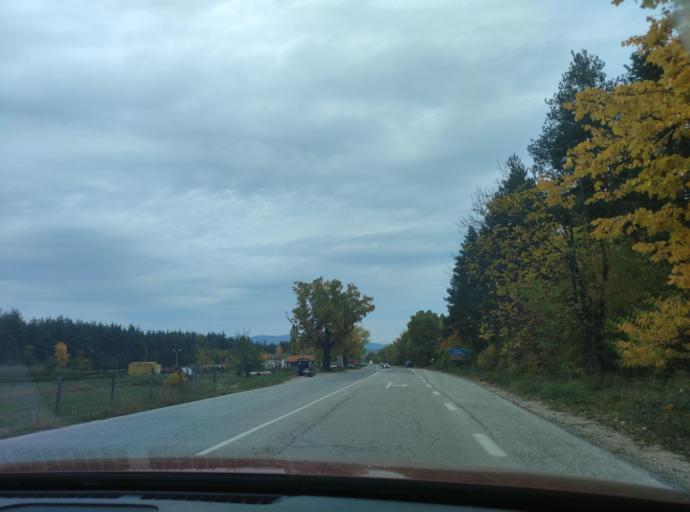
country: BG
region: Montana
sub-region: Obshtina Berkovitsa
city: Berkovitsa
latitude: 43.2179
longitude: 23.1595
